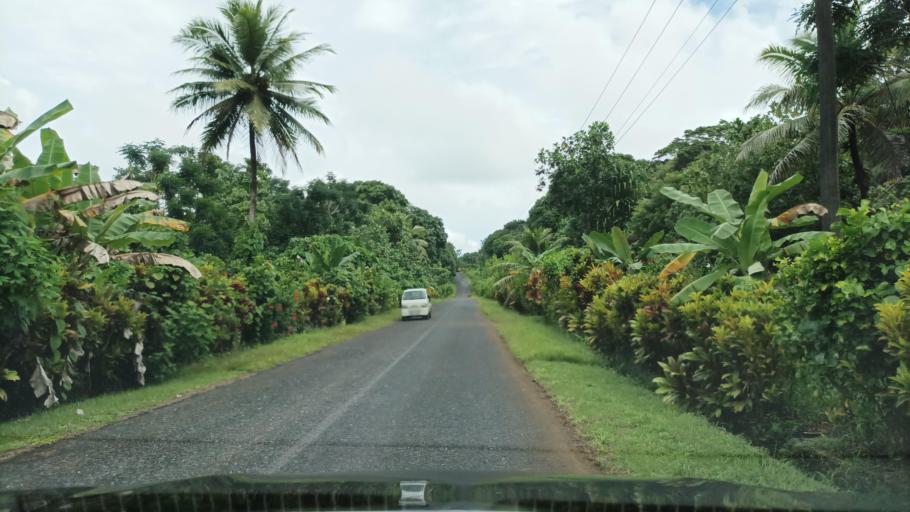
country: FM
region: Pohnpei
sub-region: Madolenihm Municipality
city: Madolenihm Municipality Government
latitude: 6.8226
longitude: 158.2975
